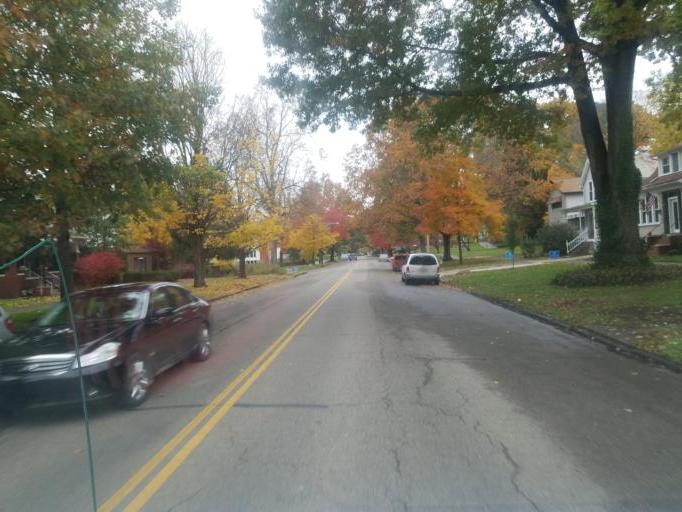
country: US
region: Ohio
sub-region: Washington County
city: Marietta
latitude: 39.4230
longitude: -81.4624
